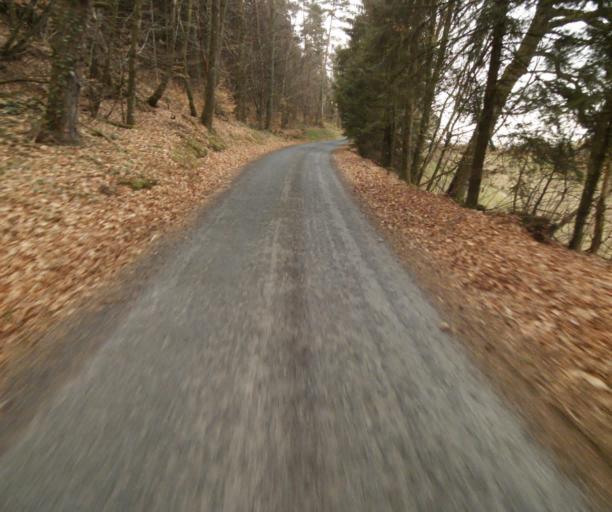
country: FR
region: Limousin
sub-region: Departement de la Correze
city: Treignac
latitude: 45.4479
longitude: 1.8196
